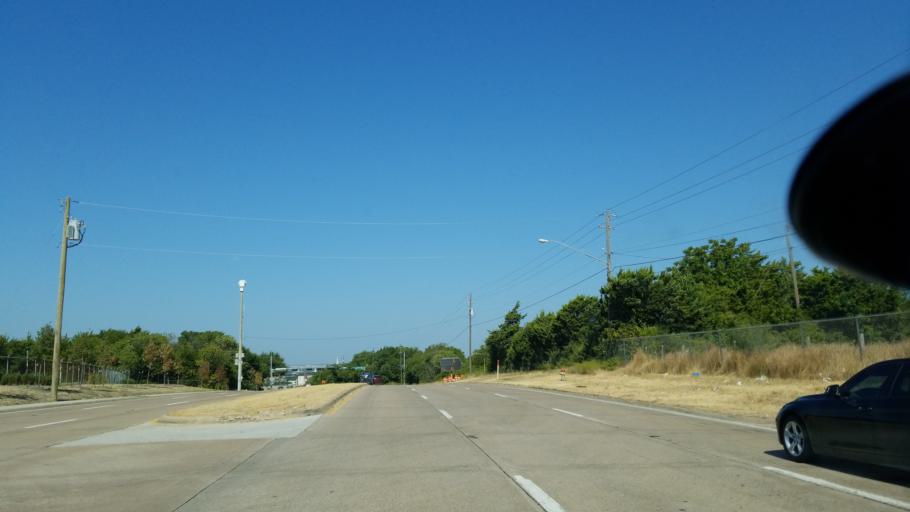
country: US
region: Texas
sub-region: Dallas County
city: Cockrell Hill
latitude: 32.7059
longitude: -96.9236
